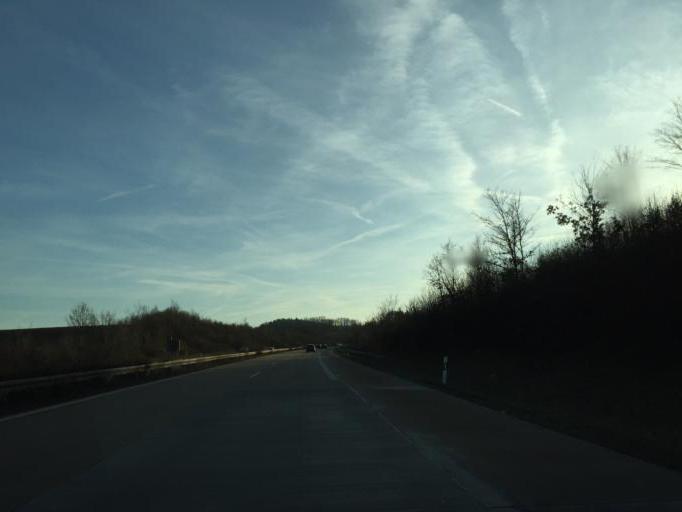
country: DE
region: Bavaria
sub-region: Regierungsbezirk Mittelfranken
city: Neusitz
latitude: 49.3462
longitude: 10.2224
